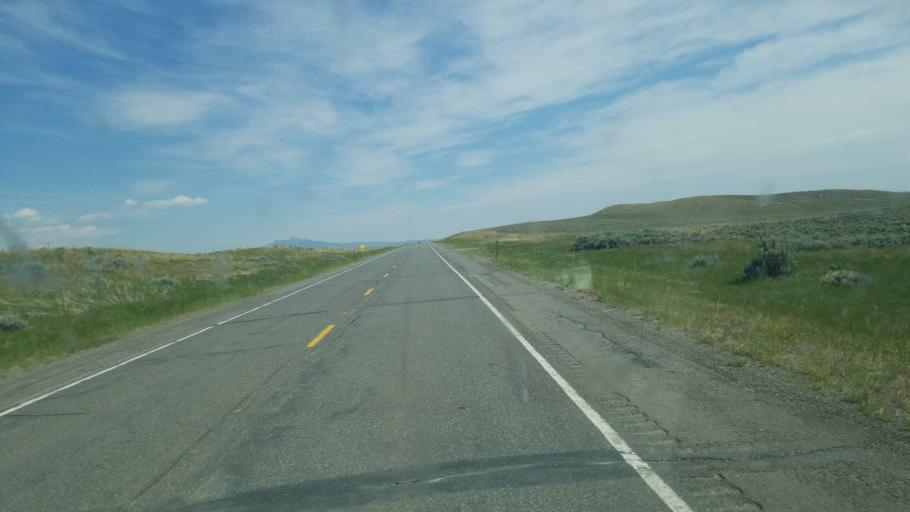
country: US
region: Wyoming
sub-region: Park County
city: Cody
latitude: 44.4266
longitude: -109.0107
